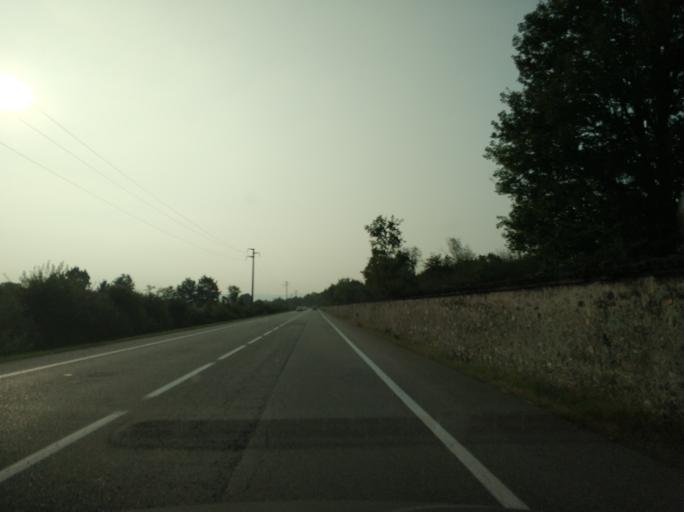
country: IT
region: Piedmont
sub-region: Provincia di Torino
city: Druento
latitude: 45.1660
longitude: 7.5962
